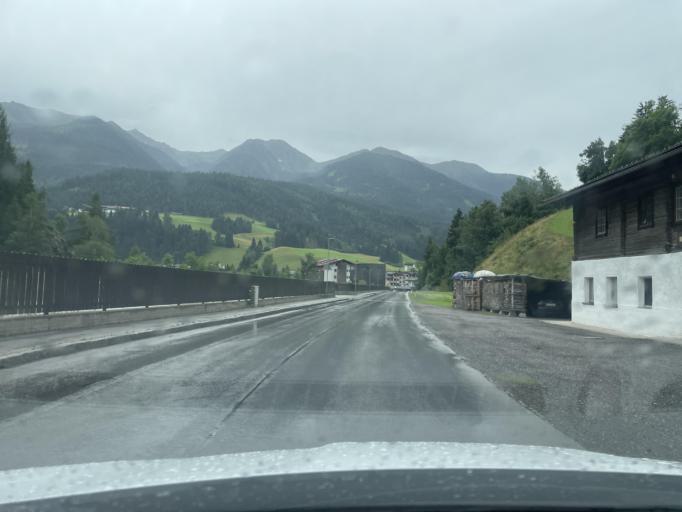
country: AT
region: Tyrol
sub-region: Politischer Bezirk Lienz
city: Heinfels
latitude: 46.7520
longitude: 12.4375
